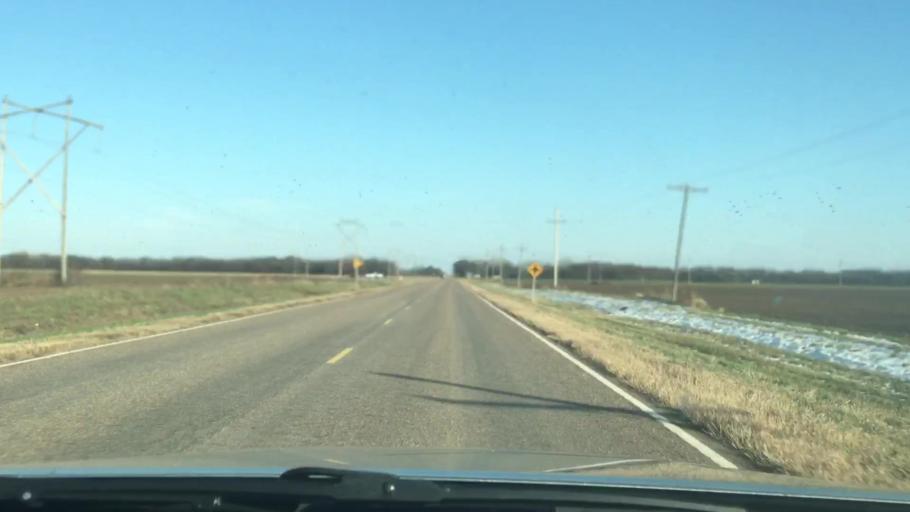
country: US
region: Kansas
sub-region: Rice County
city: Lyons
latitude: 38.2895
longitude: -98.1315
